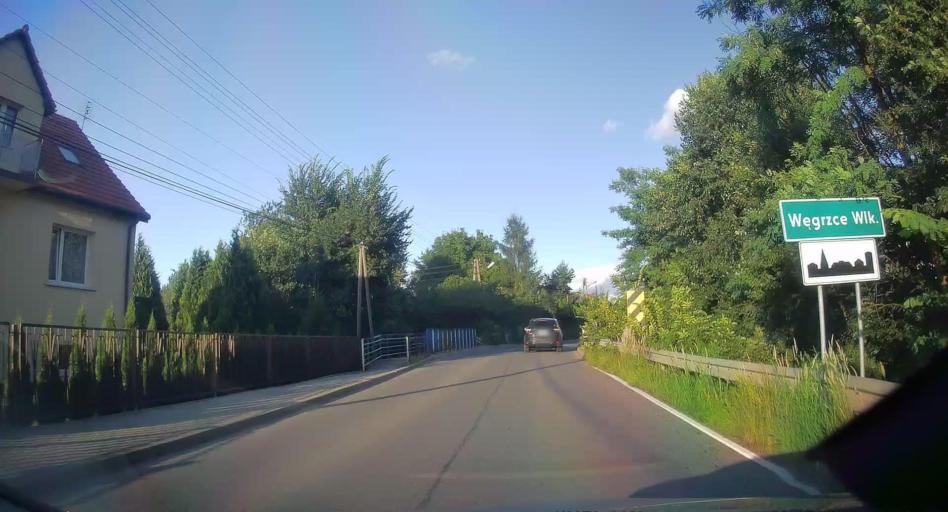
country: PL
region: Lesser Poland Voivodeship
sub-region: Powiat wielicki
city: Wegrzce Wielkie
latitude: 50.0148
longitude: 20.1025
